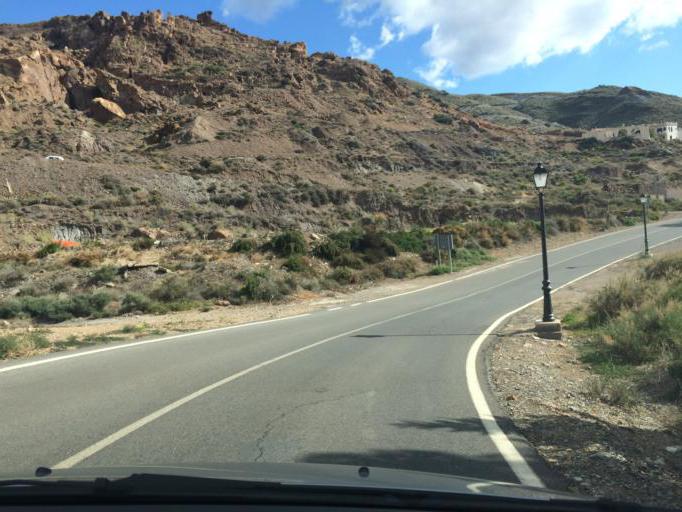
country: ES
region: Andalusia
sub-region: Provincia de Almeria
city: Pechina
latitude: 36.9613
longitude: -2.4002
